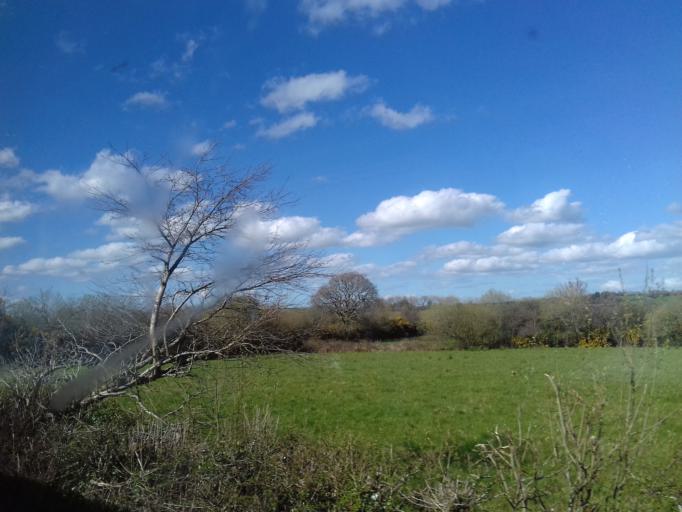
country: IE
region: Munster
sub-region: County Cork
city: Kanturk
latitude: 52.1258
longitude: -8.8193
